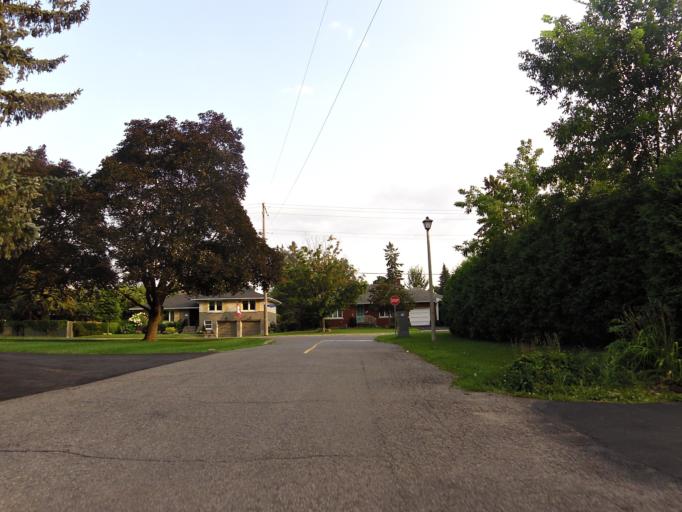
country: CA
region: Ontario
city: Ottawa
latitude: 45.3707
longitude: -75.7617
